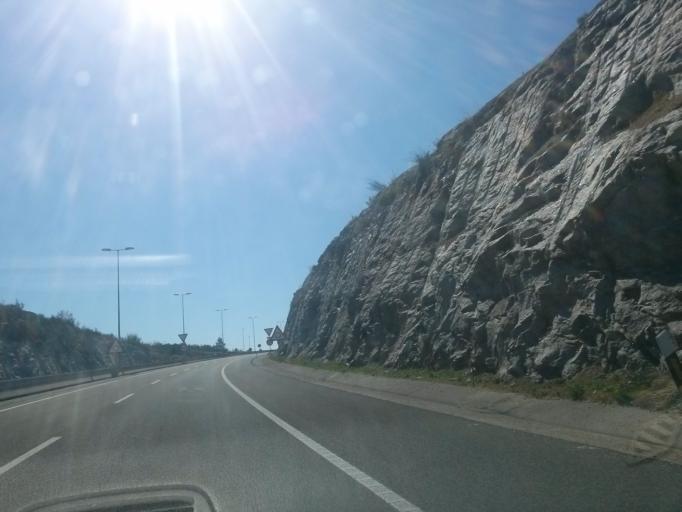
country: ES
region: Galicia
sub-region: Provincia de Lugo
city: Lugo
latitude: 43.0229
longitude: -7.5278
